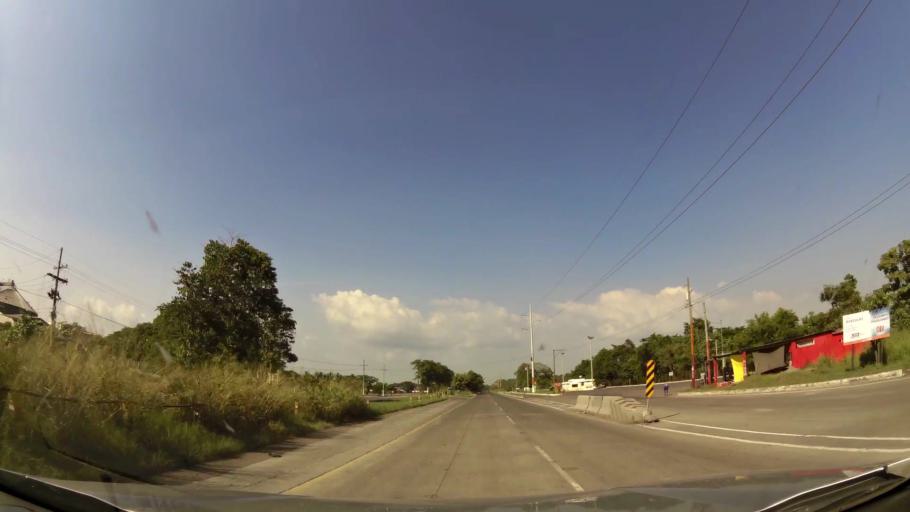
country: GT
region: Escuintla
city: Puerto San Jose
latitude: 13.9623
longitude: -90.7884
